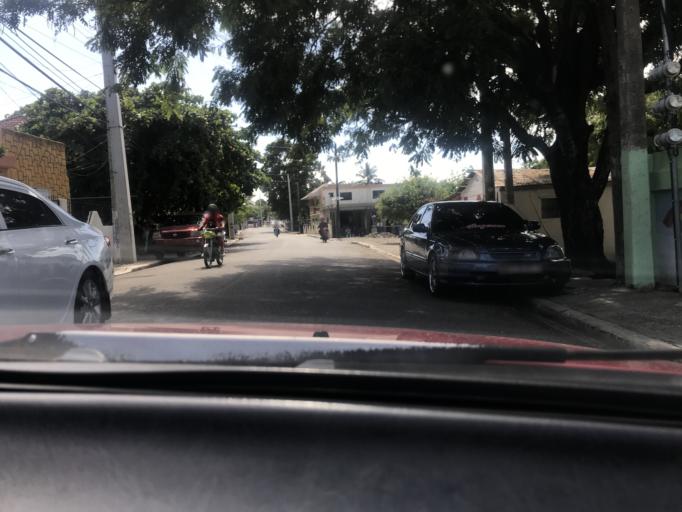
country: DO
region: Santiago
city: Licey al Medio
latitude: 19.4056
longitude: -70.6271
